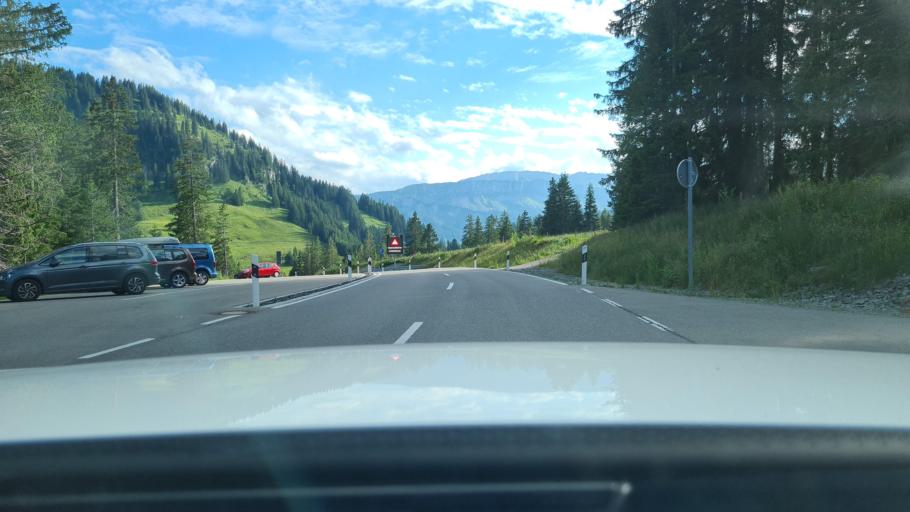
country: DE
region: Bavaria
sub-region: Swabia
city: Obermaiselstein
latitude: 47.4364
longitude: 10.1734
